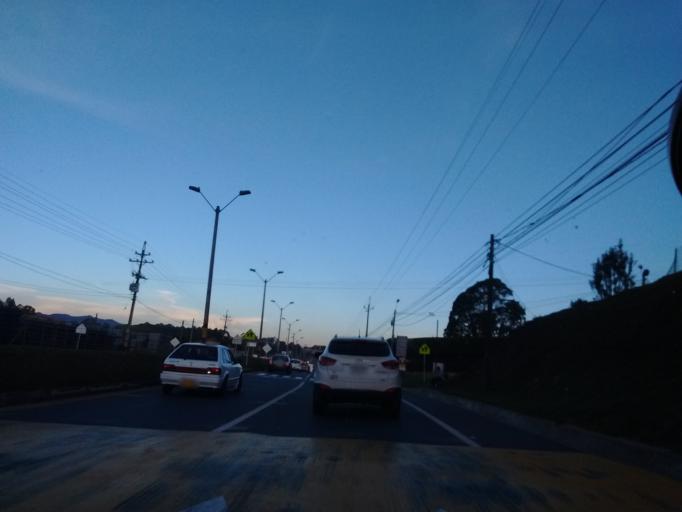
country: CO
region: Antioquia
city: Rionegro
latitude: 6.1872
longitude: -75.3793
